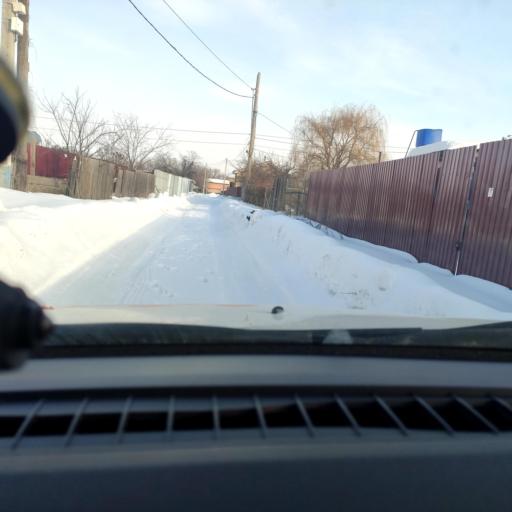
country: RU
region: Samara
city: Samara
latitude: 53.1296
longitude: 50.2566
